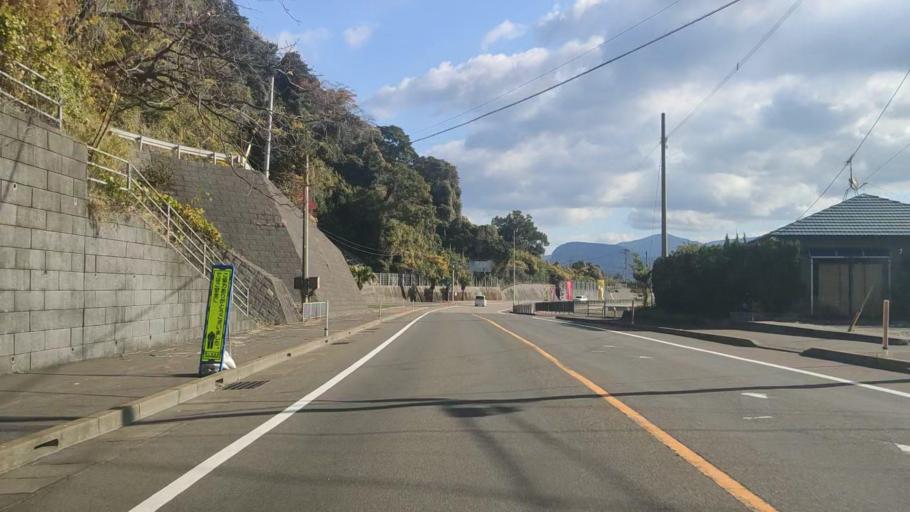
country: JP
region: Kagoshima
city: Tarumizu
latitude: 31.5513
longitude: 130.6501
